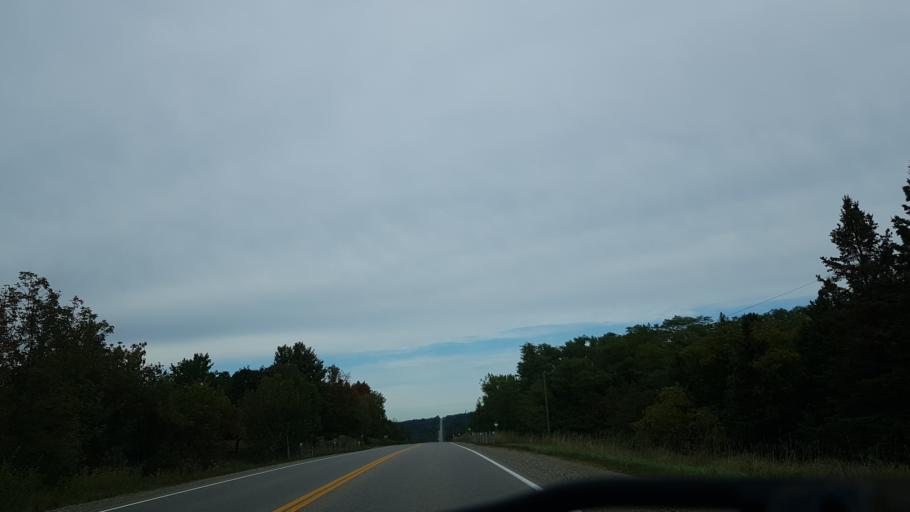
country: CA
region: Ontario
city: Orangeville
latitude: 44.0586
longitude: -80.0134
